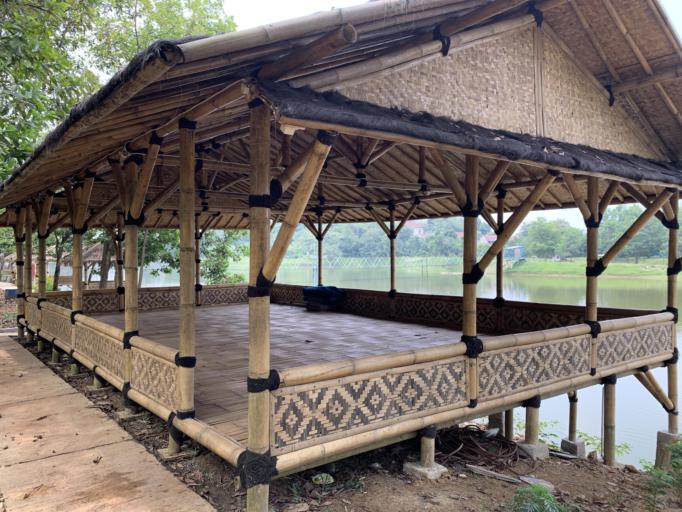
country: ID
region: West Java
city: Serpong
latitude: -6.4090
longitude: 106.5858
